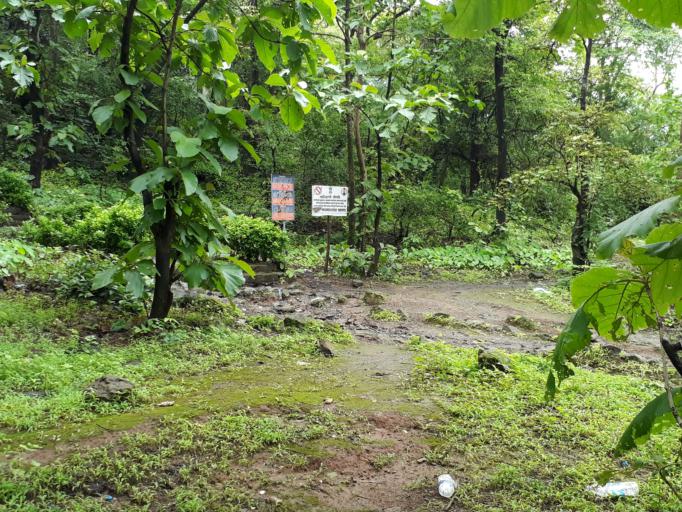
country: IN
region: Maharashtra
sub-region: Raigarh
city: Khopoli
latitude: 18.8396
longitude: 73.3840
